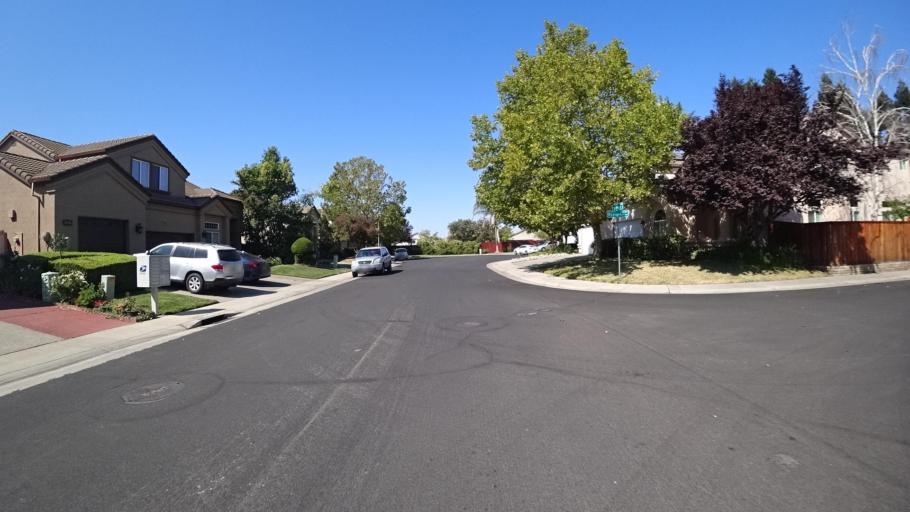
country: US
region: California
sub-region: Sacramento County
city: Vineyard
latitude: 38.4495
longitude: -121.3882
